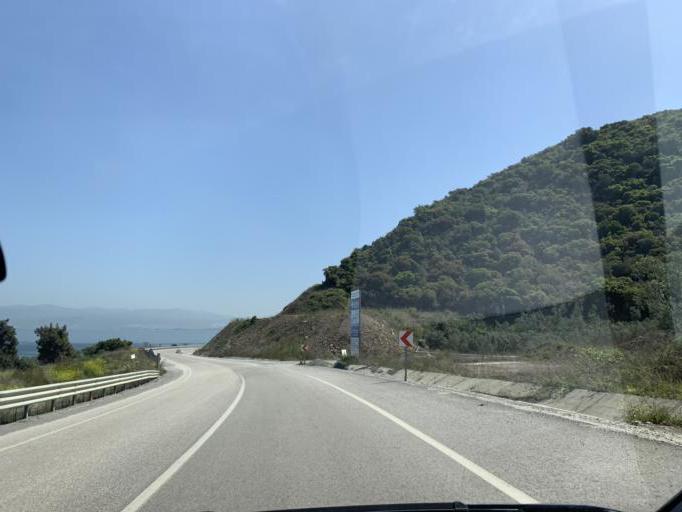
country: TR
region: Bursa
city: Niluefer
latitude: 40.3569
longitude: 28.9907
